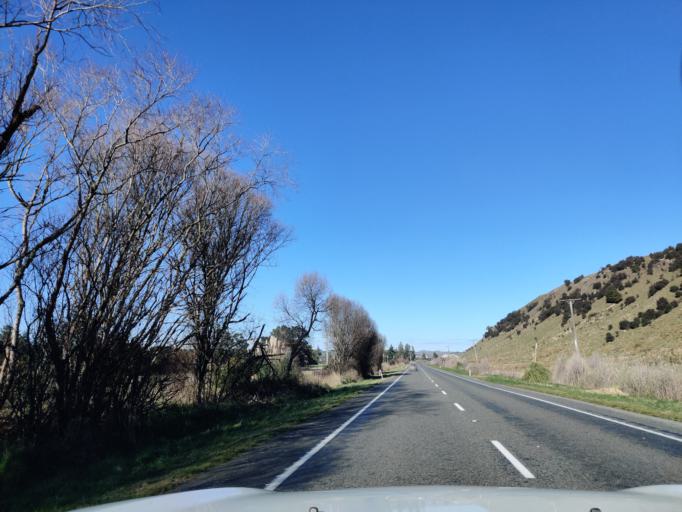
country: NZ
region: Manawatu-Wanganui
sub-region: Ruapehu District
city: Waiouru
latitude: -39.8421
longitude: 175.7415
